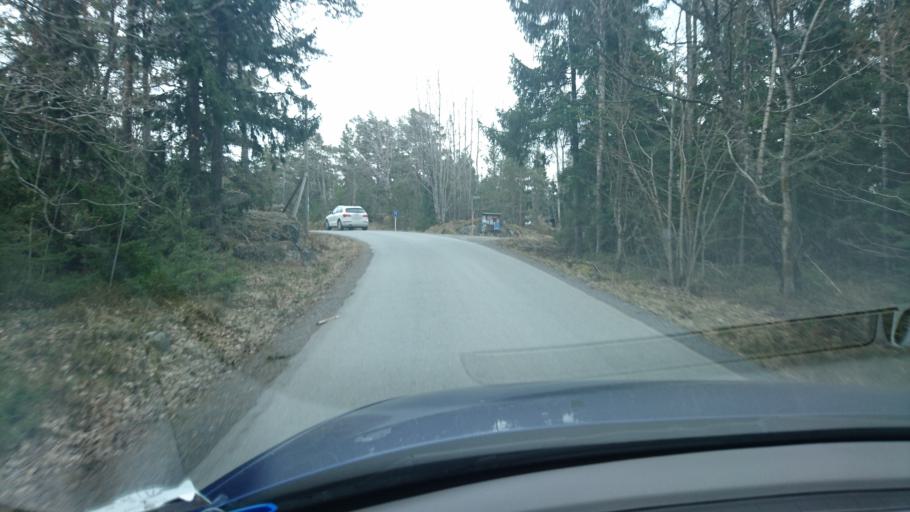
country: SE
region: Stockholm
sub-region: Norrtalje Kommun
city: Bjorko
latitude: 59.7908
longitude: 18.9863
